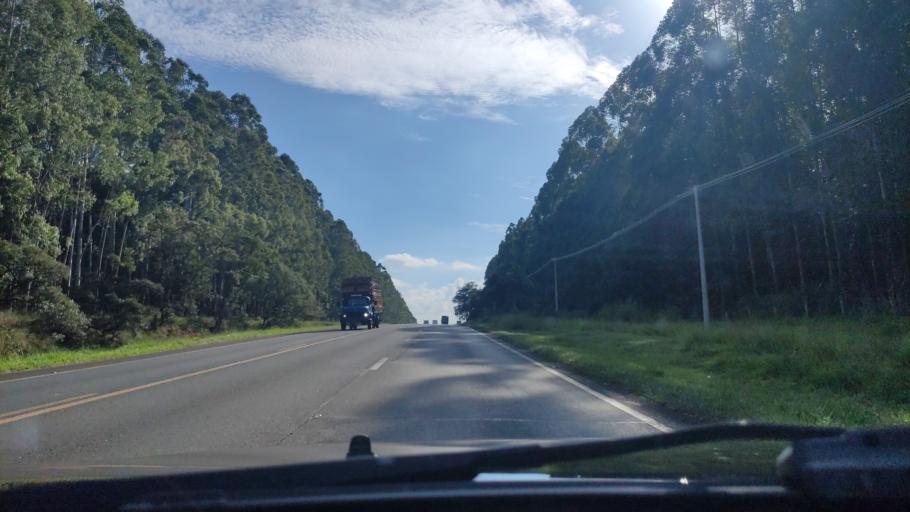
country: BR
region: Sao Paulo
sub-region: Avare
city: Avare
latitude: -22.9923
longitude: -48.8337
